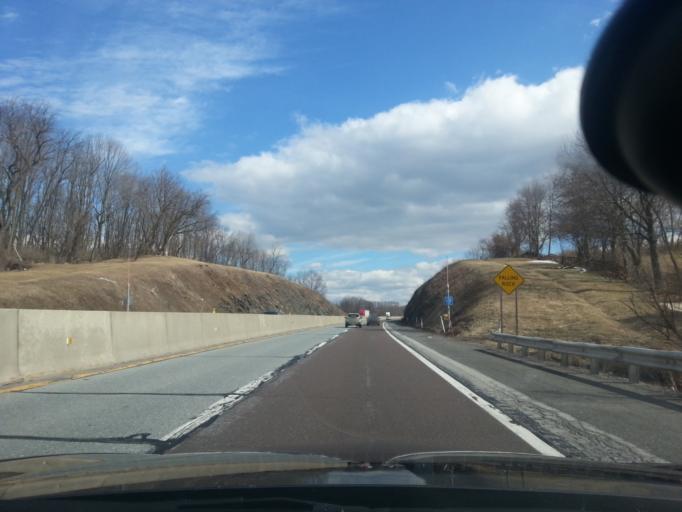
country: US
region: Pennsylvania
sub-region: Lehigh County
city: Emmaus
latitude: 40.4945
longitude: -75.4785
